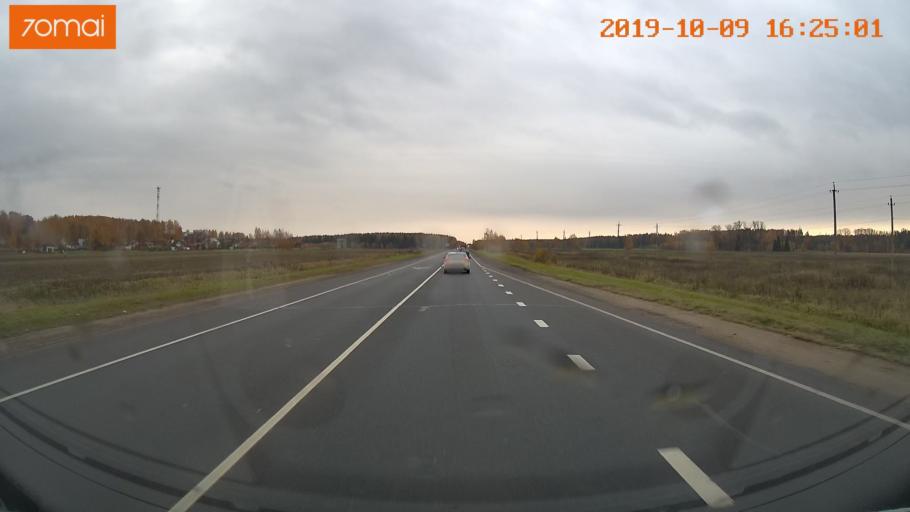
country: RU
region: Kostroma
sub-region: Kostromskoy Rayon
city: Kostroma
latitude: 57.6464
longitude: 40.9160
